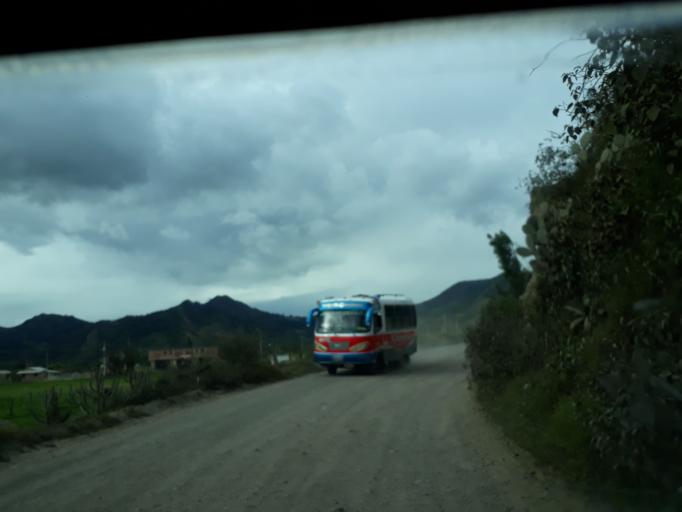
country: CO
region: Cundinamarca
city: Cucunuba
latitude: 5.2511
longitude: -73.7829
